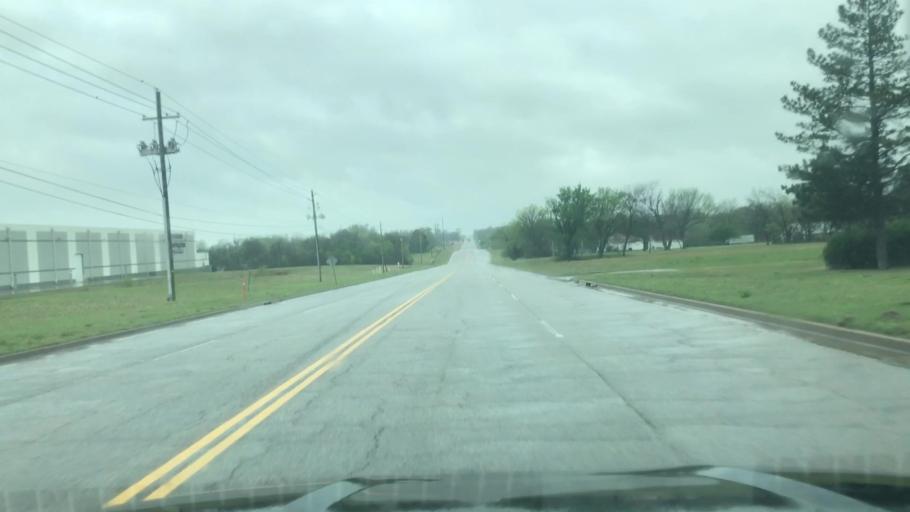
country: US
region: Oklahoma
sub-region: Tulsa County
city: Owasso
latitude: 36.2640
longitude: -95.8957
